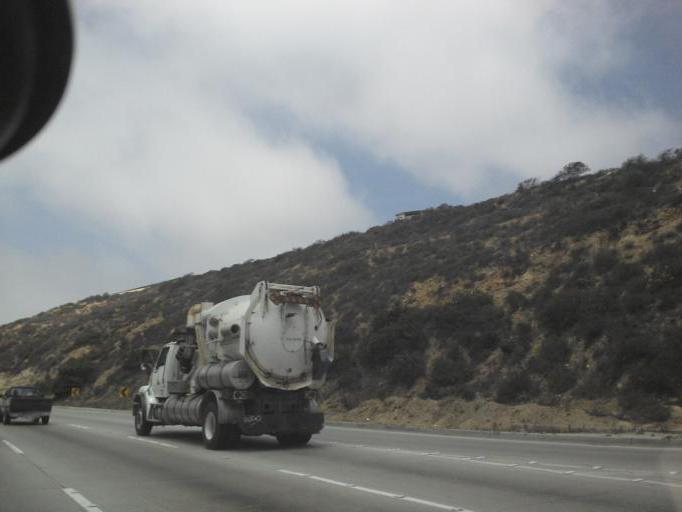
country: US
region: California
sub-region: San Diego County
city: Imperial Beach
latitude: 32.5360
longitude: -117.0915
